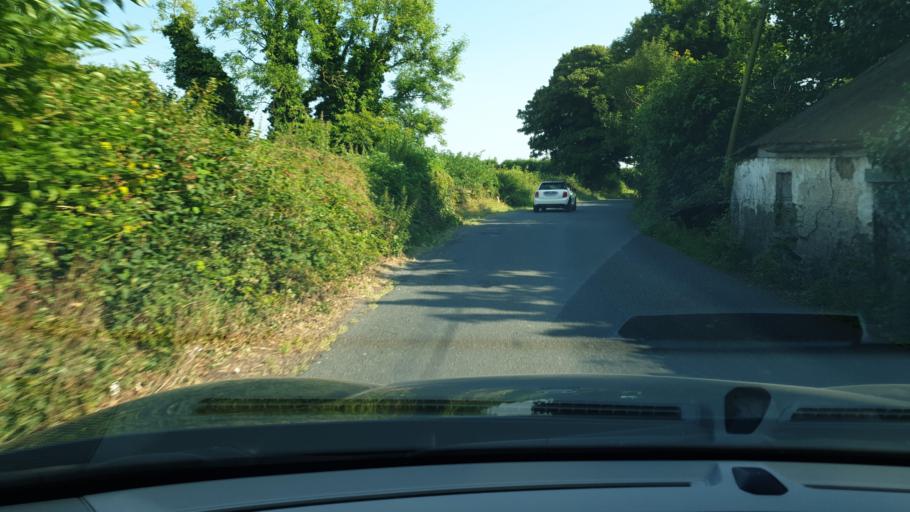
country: IE
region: Leinster
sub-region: An Mhi
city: Athboy
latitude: 53.6251
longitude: -6.9466
